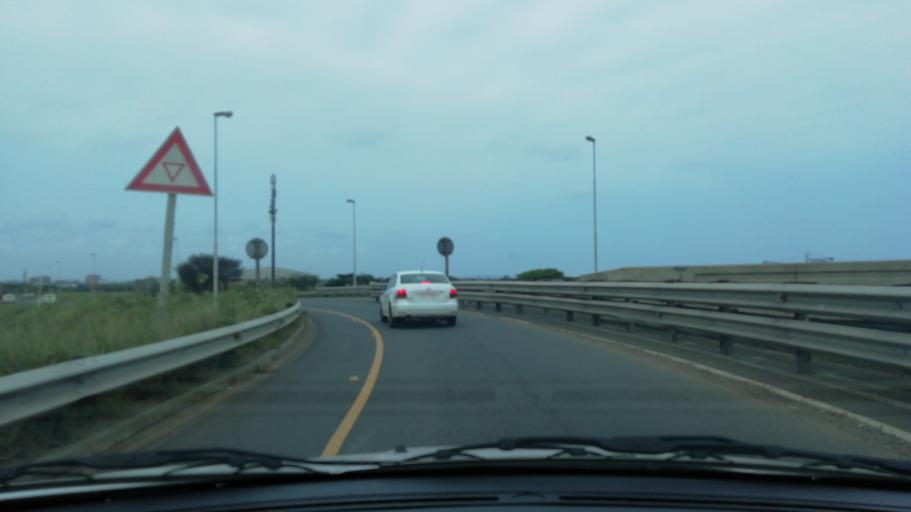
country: ZA
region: KwaZulu-Natal
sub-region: uThungulu District Municipality
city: Richards Bay
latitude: -28.7704
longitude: 32.0340
